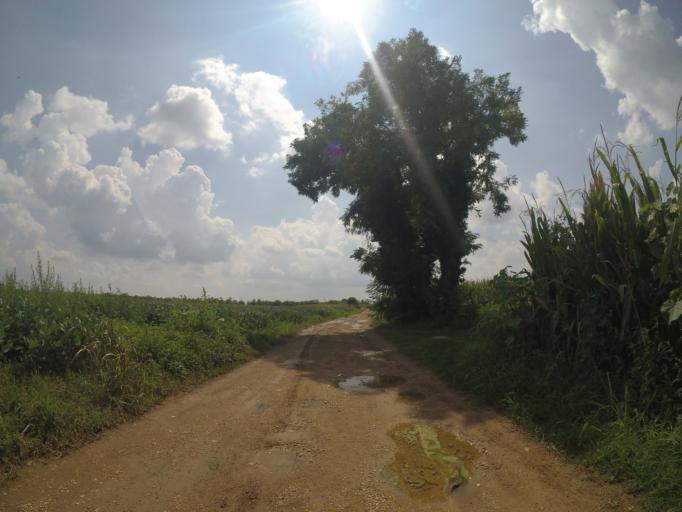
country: IT
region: Friuli Venezia Giulia
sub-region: Provincia di Udine
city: Bertiolo
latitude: 45.9617
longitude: 13.0500
